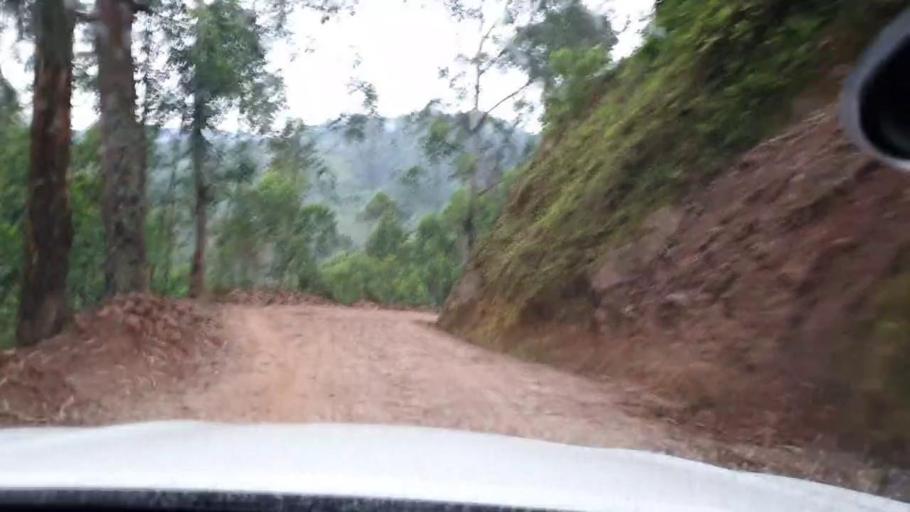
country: RW
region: Western Province
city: Cyangugu
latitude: -2.4129
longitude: 29.1973
